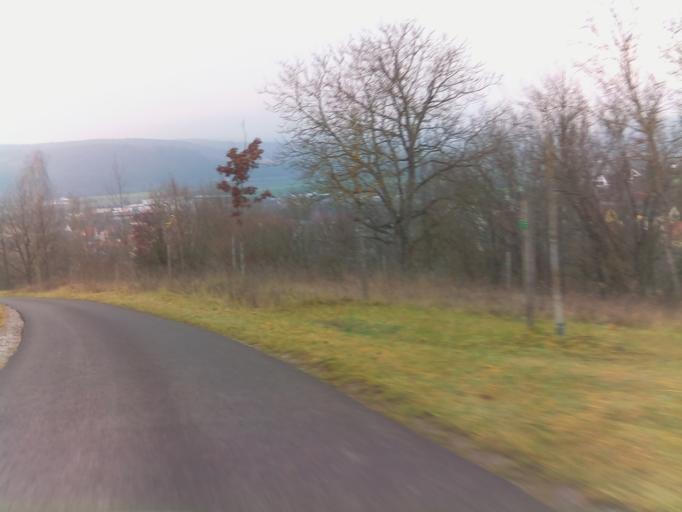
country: DE
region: Bavaria
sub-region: Regierungsbezirk Unterfranken
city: Zellingen
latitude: 49.9007
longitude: 9.8287
